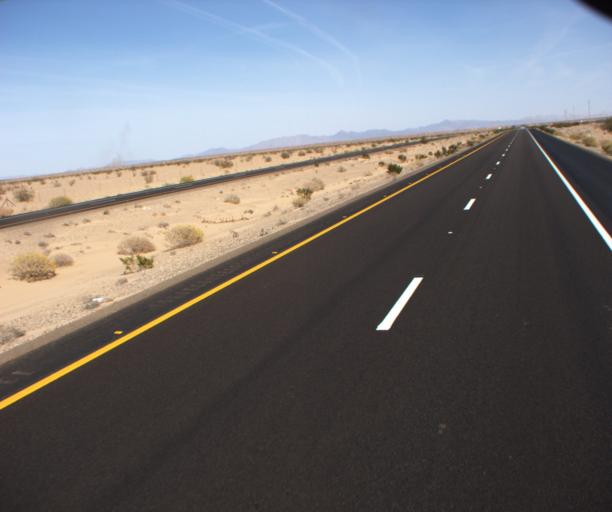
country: US
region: Arizona
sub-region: Yuma County
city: Somerton
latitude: 32.4951
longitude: -114.6367
